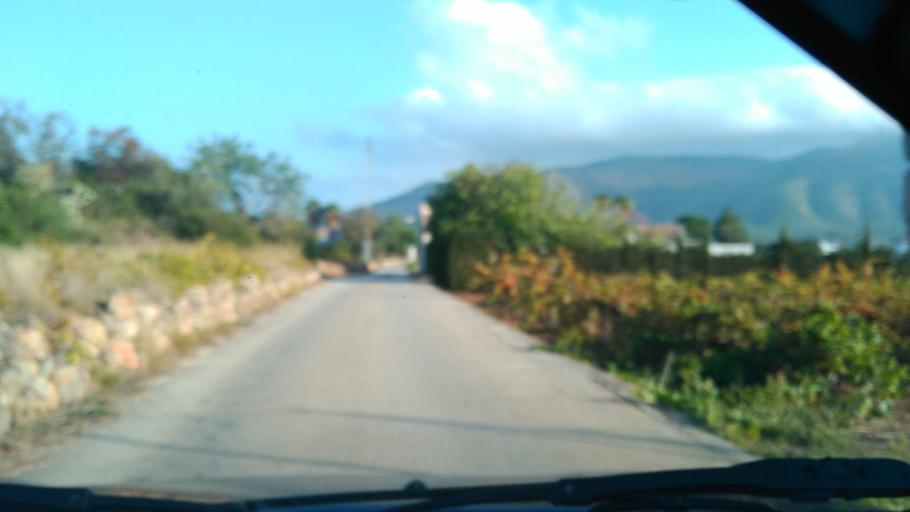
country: ES
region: Valencia
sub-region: Provincia de Alicante
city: Gata de Gorgos
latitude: 38.7847
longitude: 0.0894
